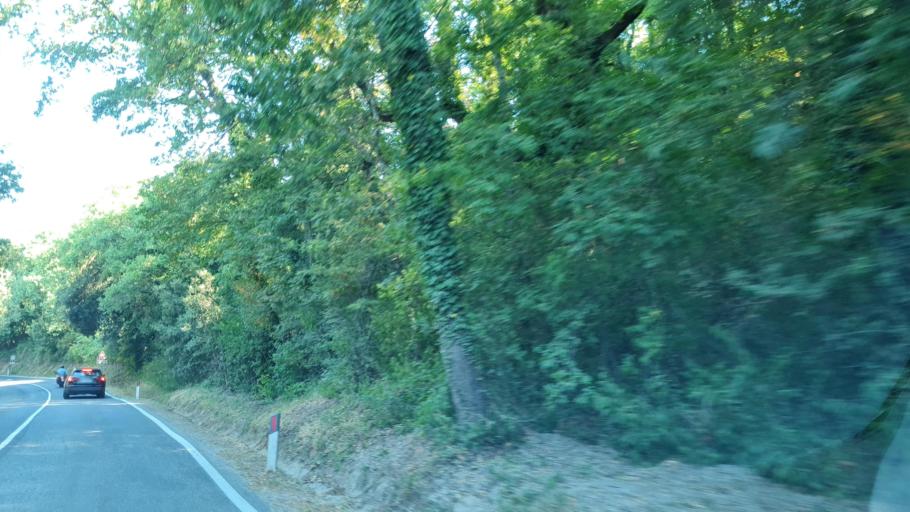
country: IT
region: Tuscany
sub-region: Provincia di Siena
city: Chianciano Terme
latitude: 43.0266
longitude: 11.7767
